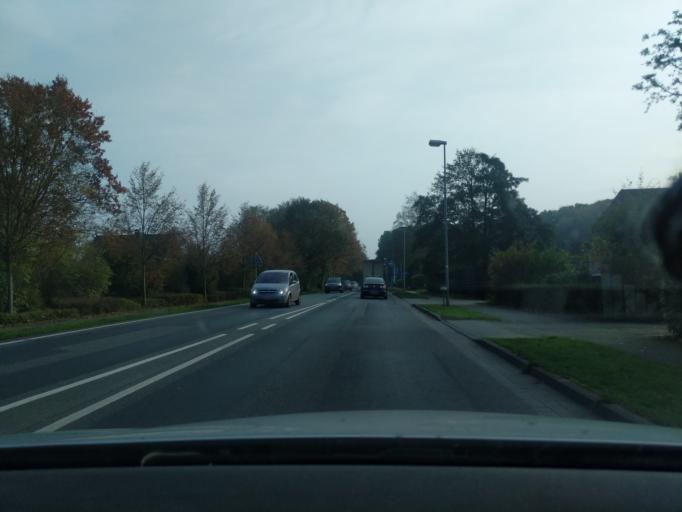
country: DE
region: Lower Saxony
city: Himmelpforten
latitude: 53.6118
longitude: 9.3130
